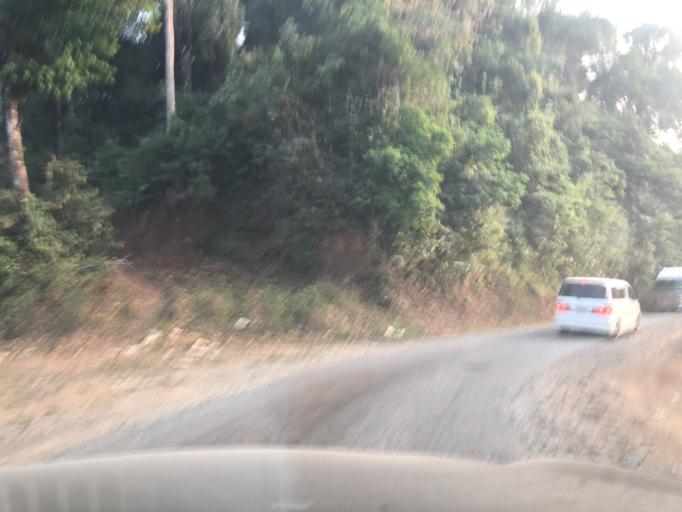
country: MM
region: Bago
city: Pyay
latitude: 18.7147
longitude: 94.5427
